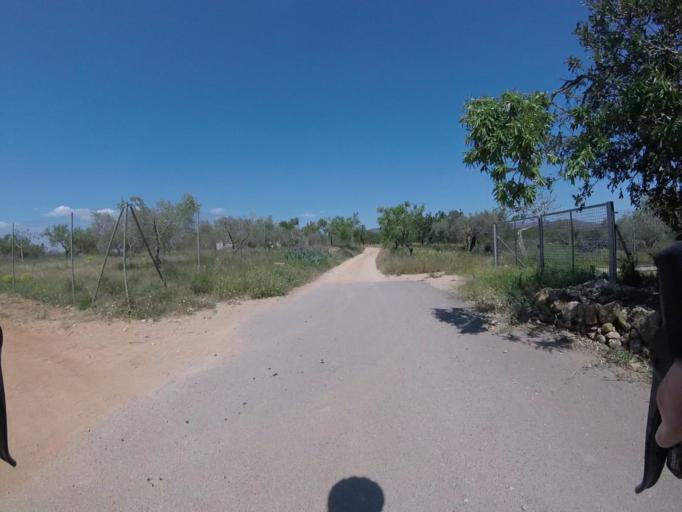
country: ES
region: Valencia
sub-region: Provincia de Castello
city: Benlloch
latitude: 40.2006
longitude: -0.0113
